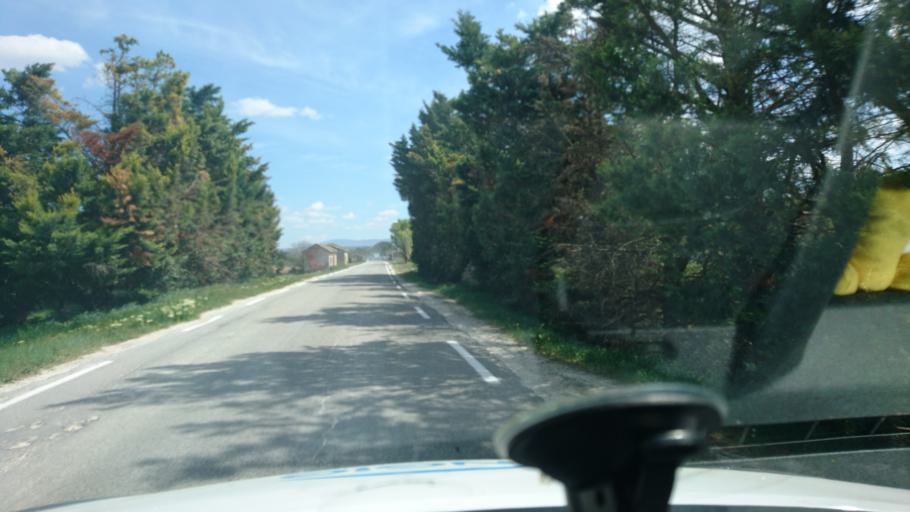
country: FR
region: Provence-Alpes-Cote d'Azur
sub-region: Departement du Vaucluse
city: Maubec
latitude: 43.8604
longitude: 5.1401
